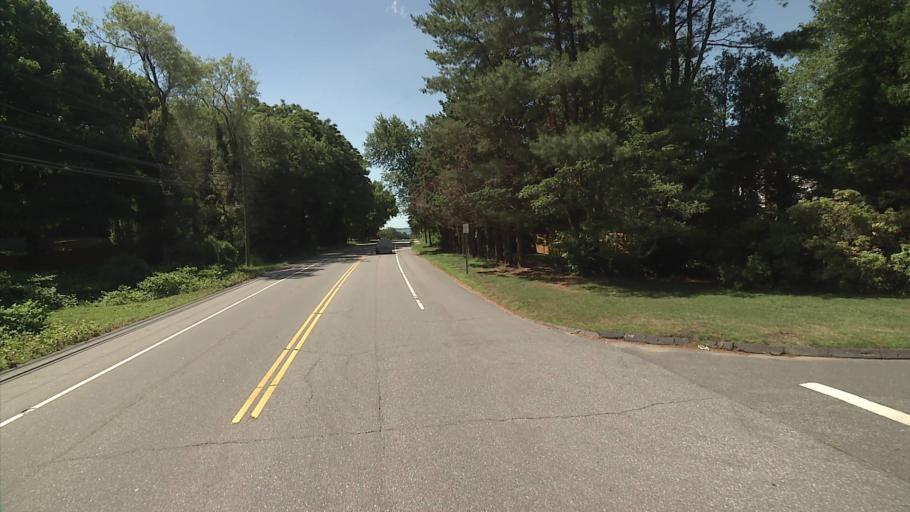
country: US
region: Connecticut
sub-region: New London County
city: Noank
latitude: 41.3281
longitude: -71.9985
